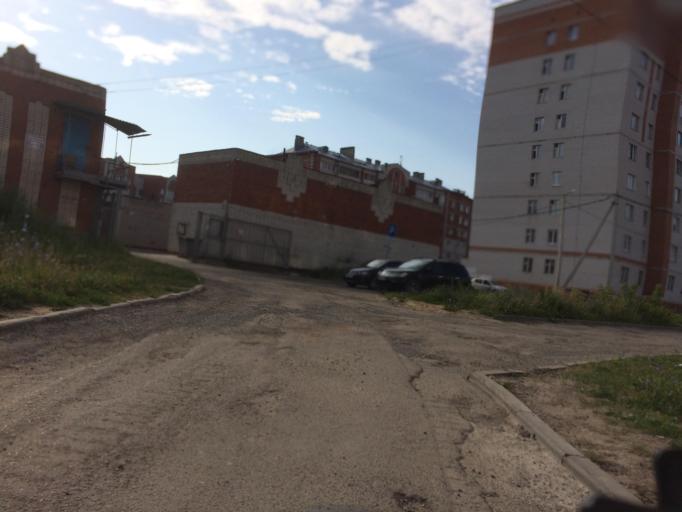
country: RU
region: Mariy-El
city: Medvedevo
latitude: 56.6386
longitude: 47.8259
